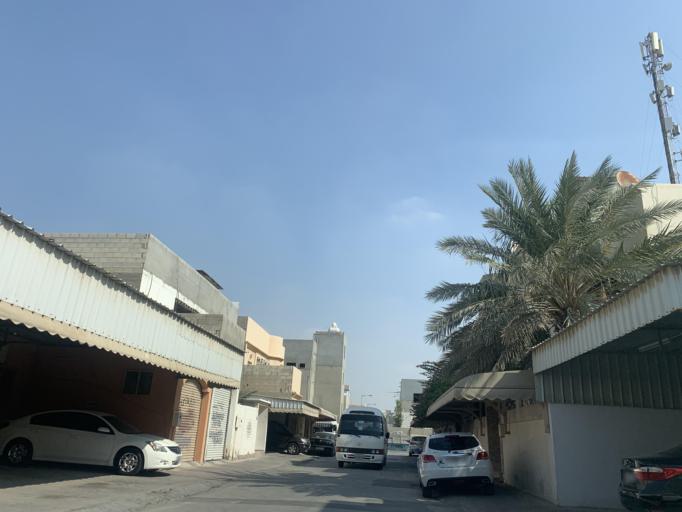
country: BH
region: Central Governorate
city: Madinat Hamad
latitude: 26.1288
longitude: 50.4933
